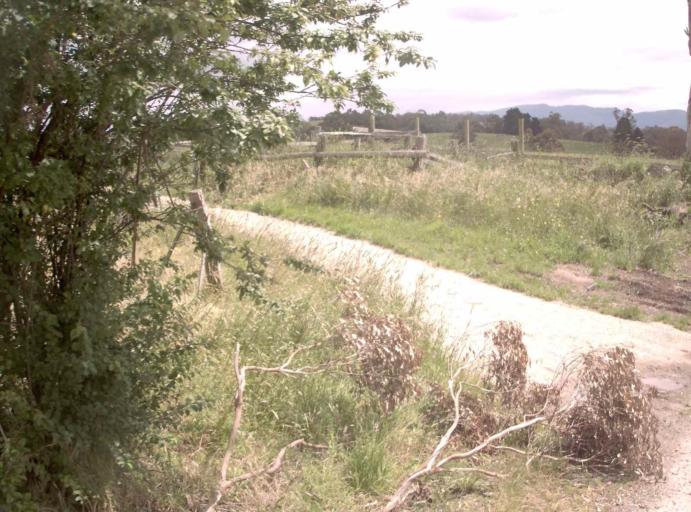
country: AU
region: Victoria
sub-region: Latrobe
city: Moe
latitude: -38.0004
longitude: 146.1443
